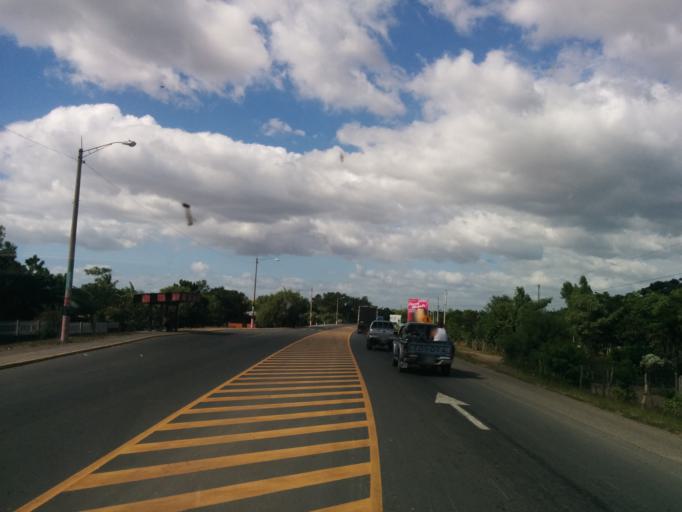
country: NI
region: Matagalpa
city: Ciudad Dario
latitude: 12.6663
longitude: -86.0875
